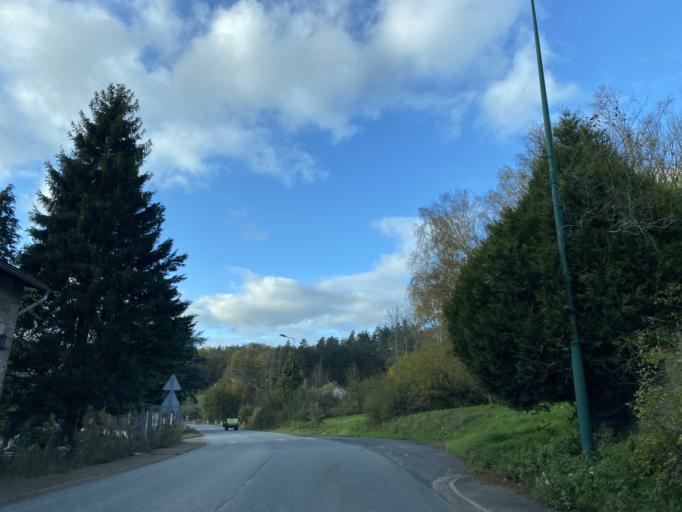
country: FR
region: Auvergne
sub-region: Departement du Puy-de-Dome
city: Job
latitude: 45.6469
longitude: 3.7001
